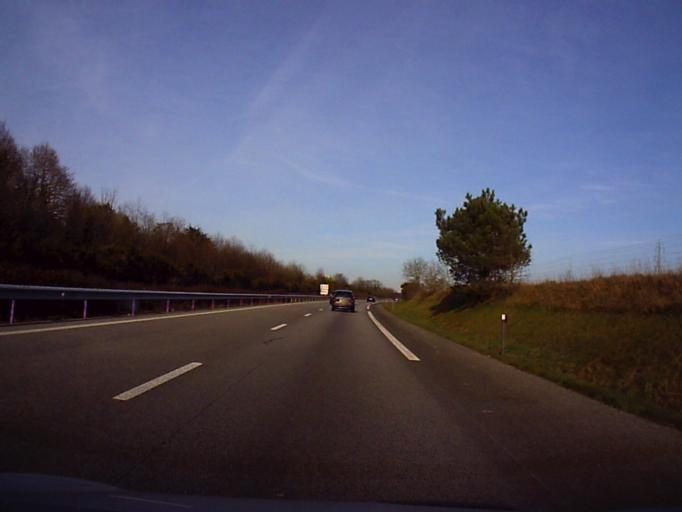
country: FR
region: Brittany
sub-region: Departement du Morbihan
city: Elven
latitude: 47.7576
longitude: -2.5439
